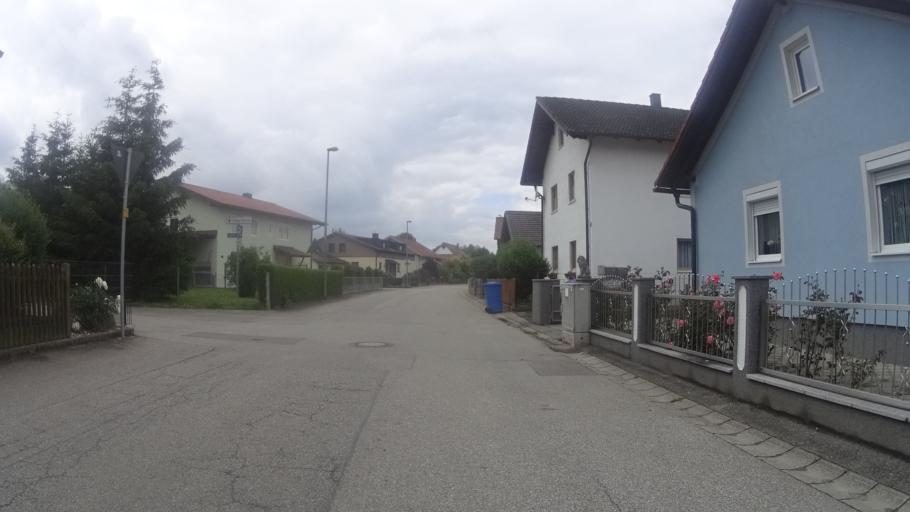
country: DE
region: Bavaria
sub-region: Lower Bavaria
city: Pfarrkirchen
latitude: 48.4254
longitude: 12.9372
